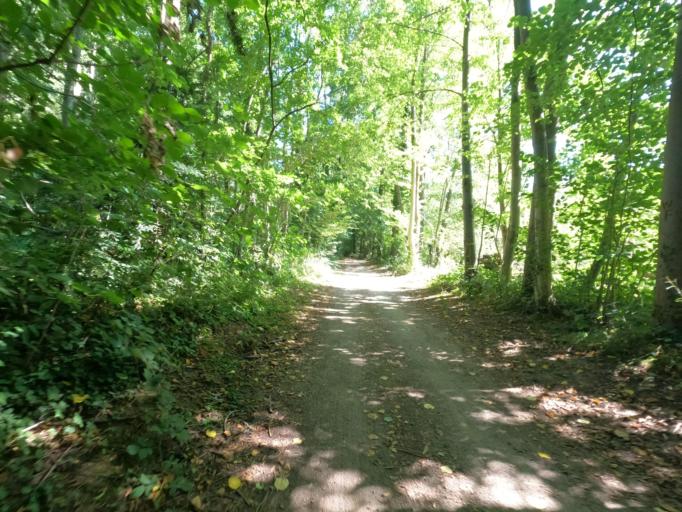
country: DE
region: North Rhine-Westphalia
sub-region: Regierungsbezirk Koln
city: Linnich
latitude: 50.9546
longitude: 6.2952
